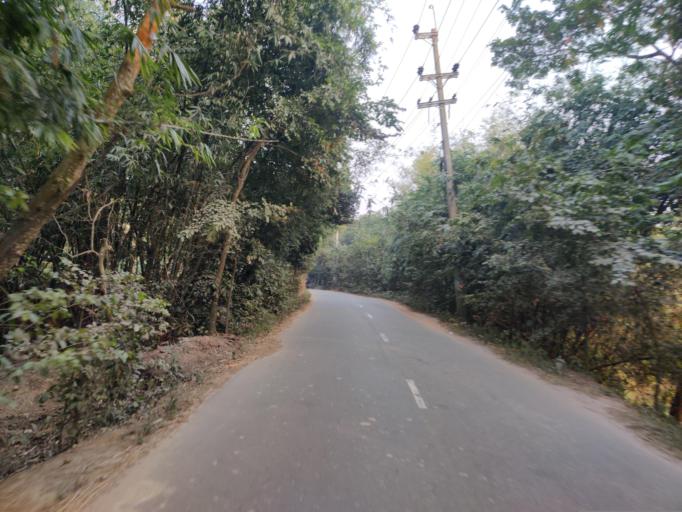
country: BD
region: Dhaka
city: Bajitpur
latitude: 24.1575
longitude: 90.7654
